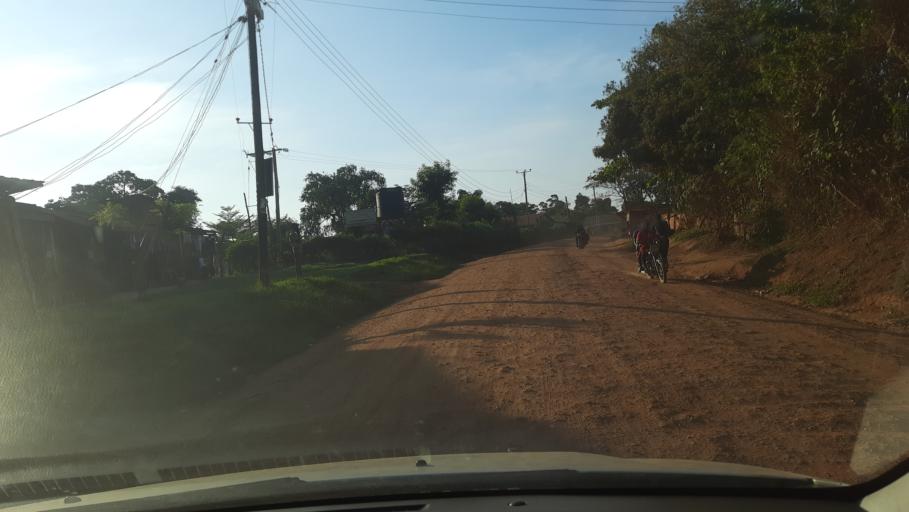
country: UG
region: Central Region
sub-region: Mukono District
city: Mukono
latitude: 0.3727
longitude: 32.7484
